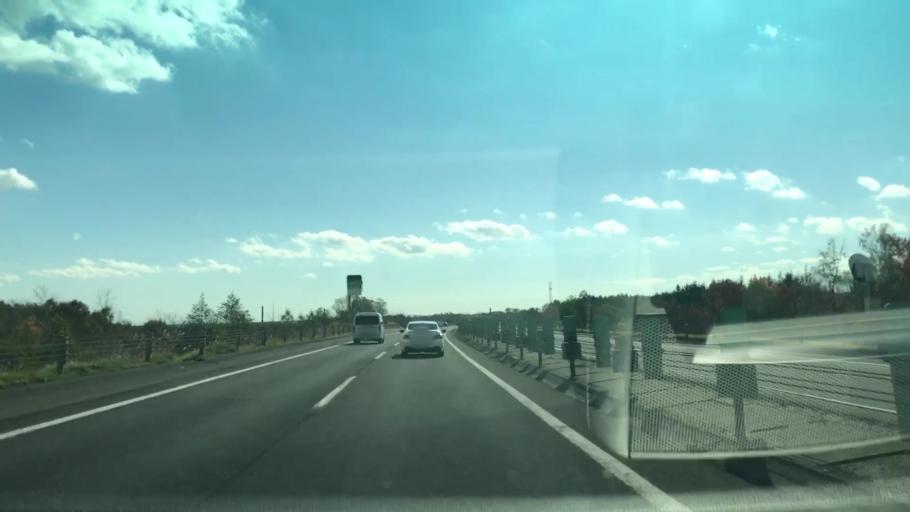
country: JP
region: Hokkaido
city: Kitahiroshima
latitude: 42.9079
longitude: 141.5505
